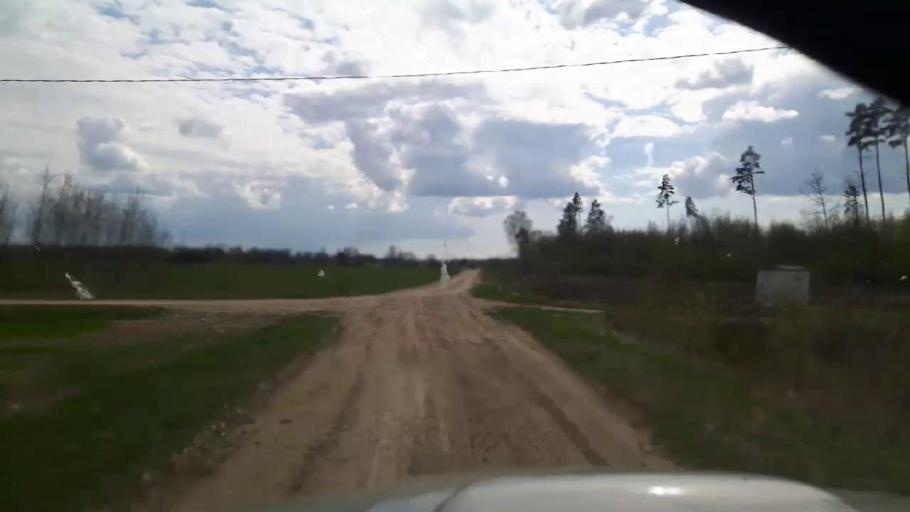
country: EE
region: Paernumaa
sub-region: Tootsi vald
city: Tootsi
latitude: 58.5154
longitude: 24.8483
